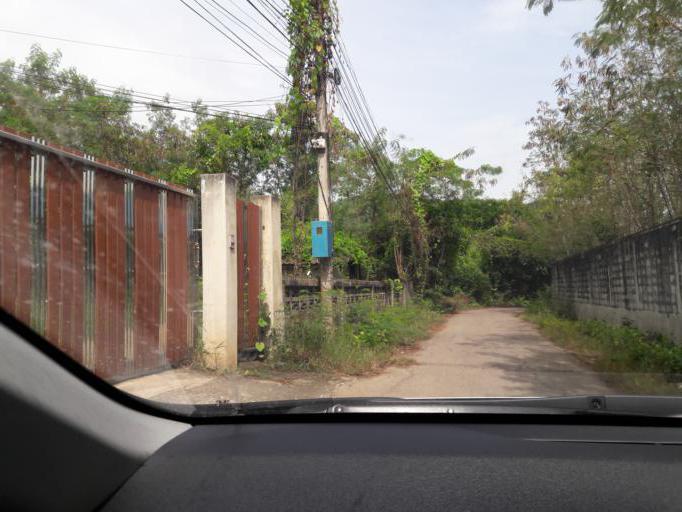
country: TH
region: Ratchaburi
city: Ratchaburi
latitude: 13.5218
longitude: 99.7934
